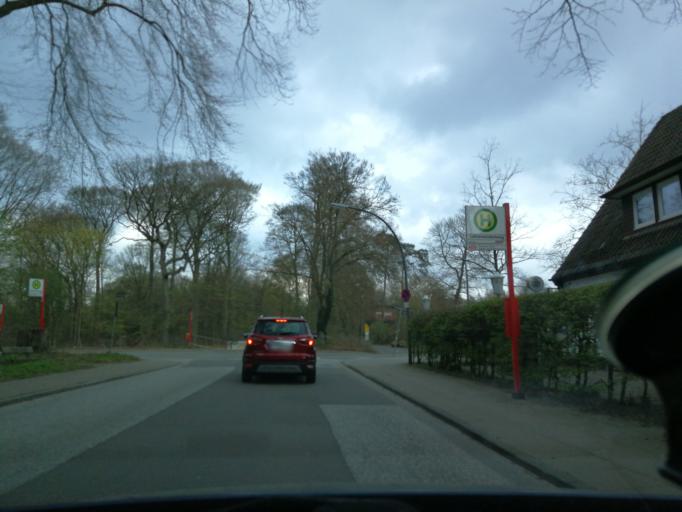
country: DE
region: Hamburg
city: Harburg
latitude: 53.4599
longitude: 9.9349
